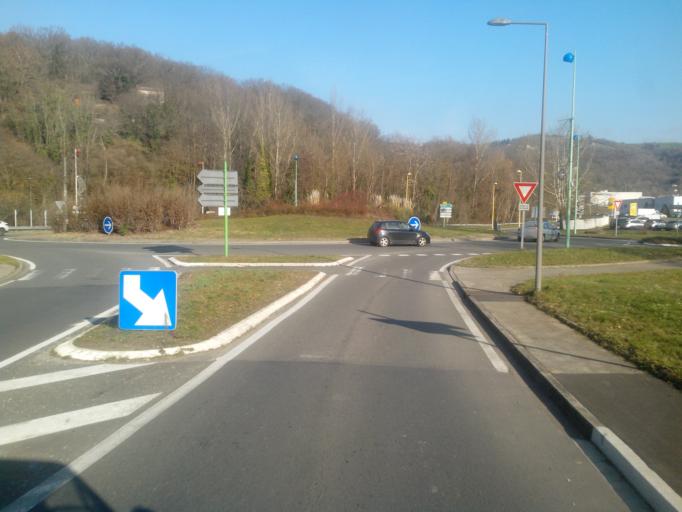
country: FR
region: Midi-Pyrenees
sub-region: Departement de l'Aveyron
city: Decazeville
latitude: 44.5565
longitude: 2.2645
